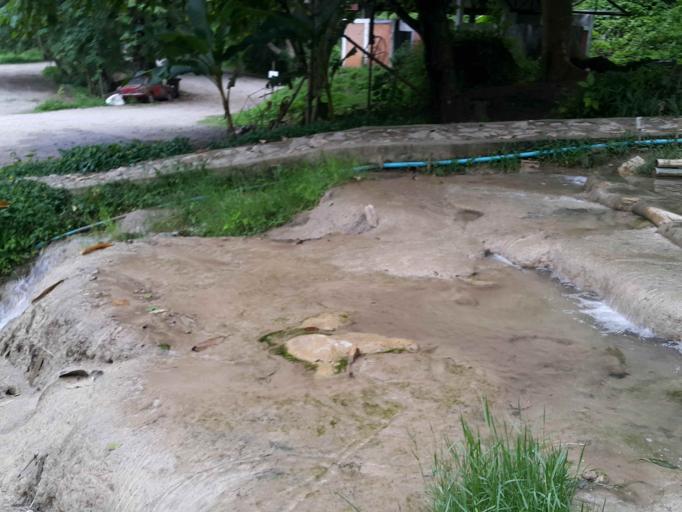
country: TH
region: Lampang
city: Wang Nuea
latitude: 19.0701
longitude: 99.7291
